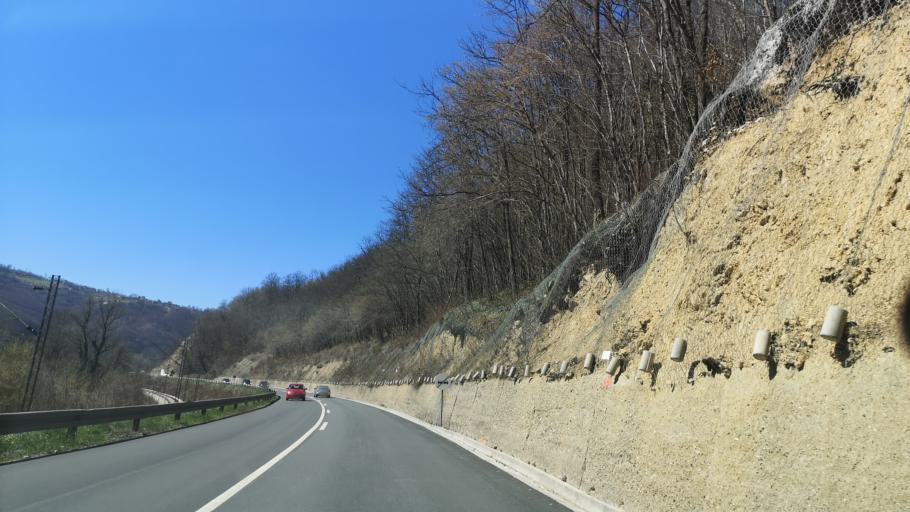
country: RS
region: Central Serbia
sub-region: Moravicki Okrug
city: Lucani
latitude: 43.8996
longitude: 20.1605
